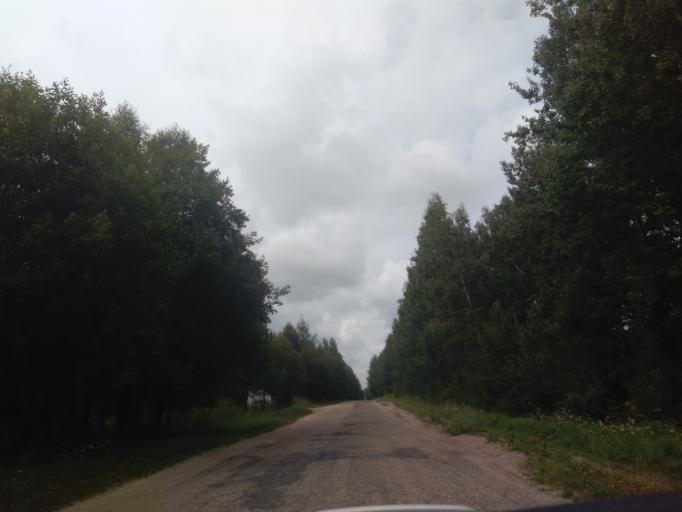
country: BY
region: Minsk
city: Slabada
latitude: 53.9933
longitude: 27.9140
